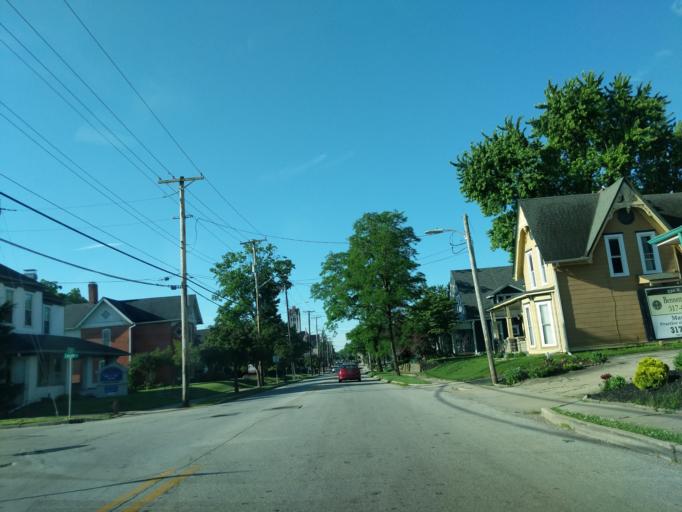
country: US
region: Indiana
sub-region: Hancock County
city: Greenfield
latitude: 39.7890
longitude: -85.7695
